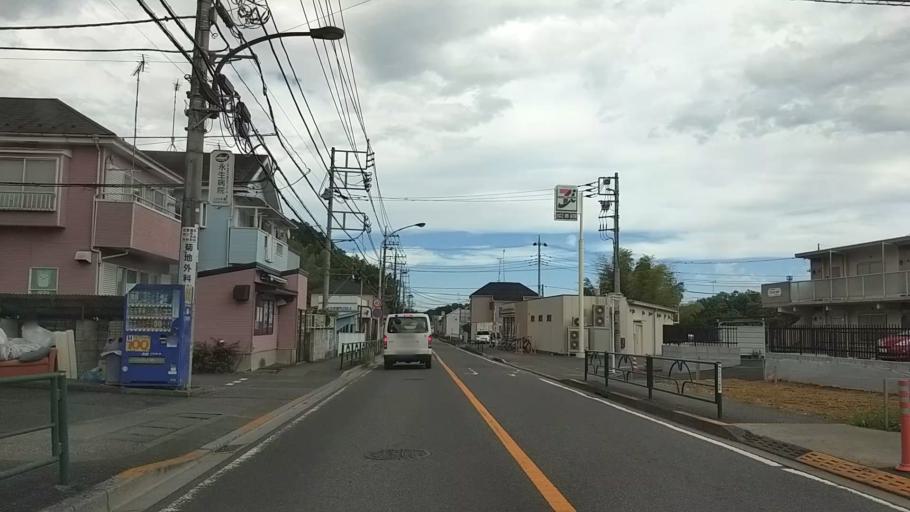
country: JP
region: Tokyo
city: Hachioji
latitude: 35.6356
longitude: 139.3003
